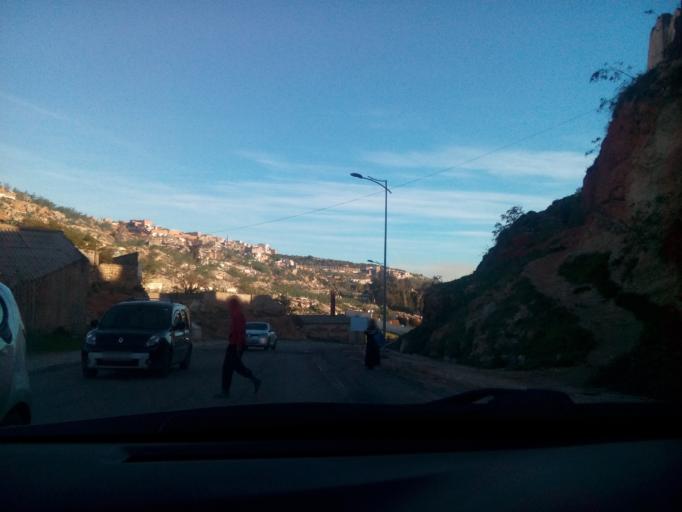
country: DZ
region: Oran
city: Oran
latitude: 35.6903
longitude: -0.6667
